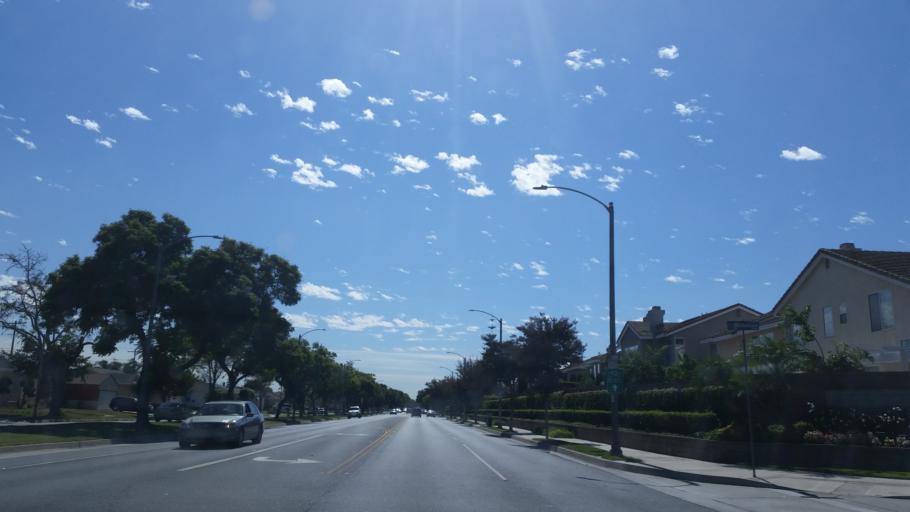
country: US
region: California
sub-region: Los Angeles County
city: Lakewood
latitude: 33.8570
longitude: -118.1512
